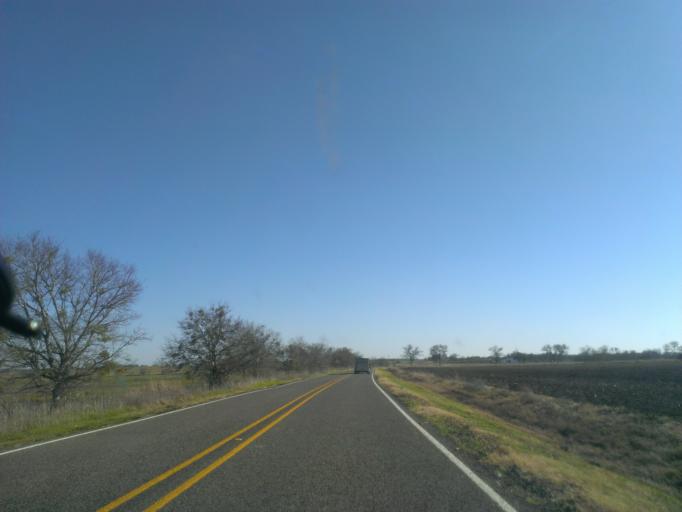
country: US
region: Texas
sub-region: Milam County
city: Thorndale
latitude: 30.5314
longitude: -97.2534
